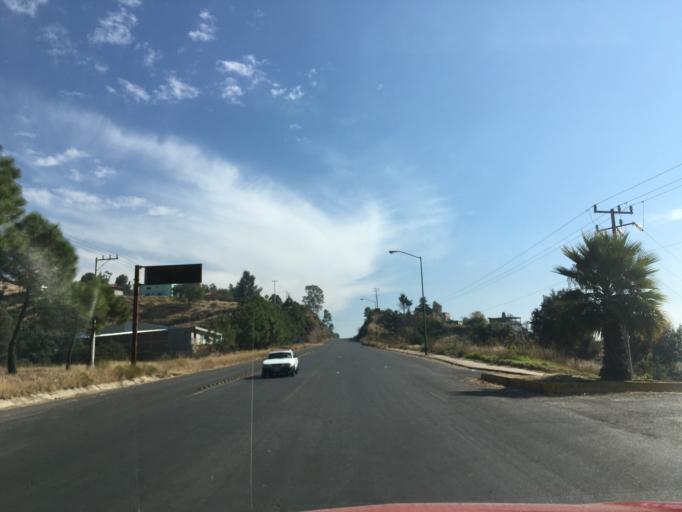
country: MX
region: Michoacan
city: Ciudad Hidalgo
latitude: 19.7072
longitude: -100.5551
